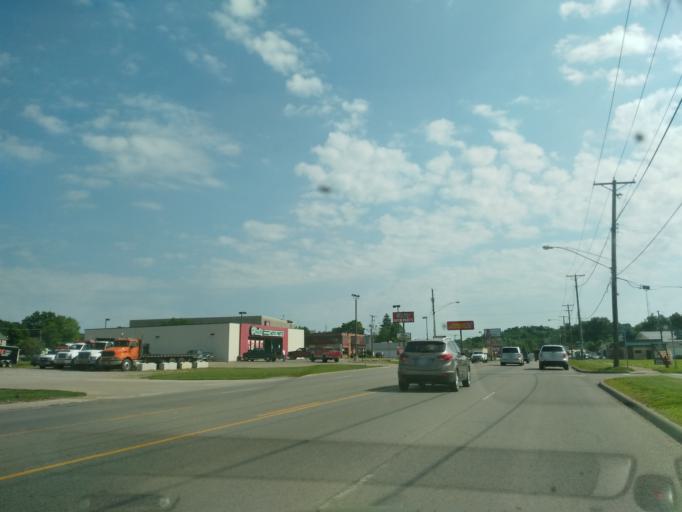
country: US
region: Ohio
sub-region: Muskingum County
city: South Zanesville
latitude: 39.9056
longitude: -82.0190
